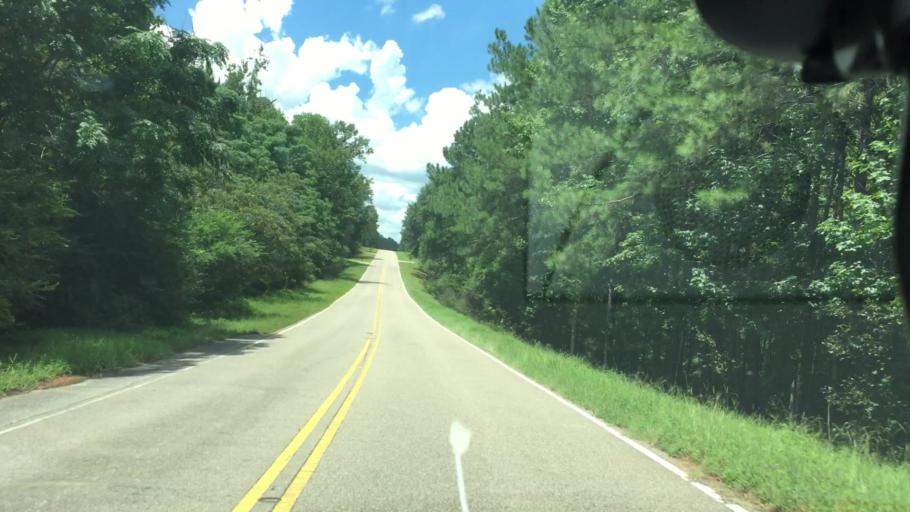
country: US
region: Alabama
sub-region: Coffee County
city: New Brockton
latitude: 31.4088
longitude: -85.8443
